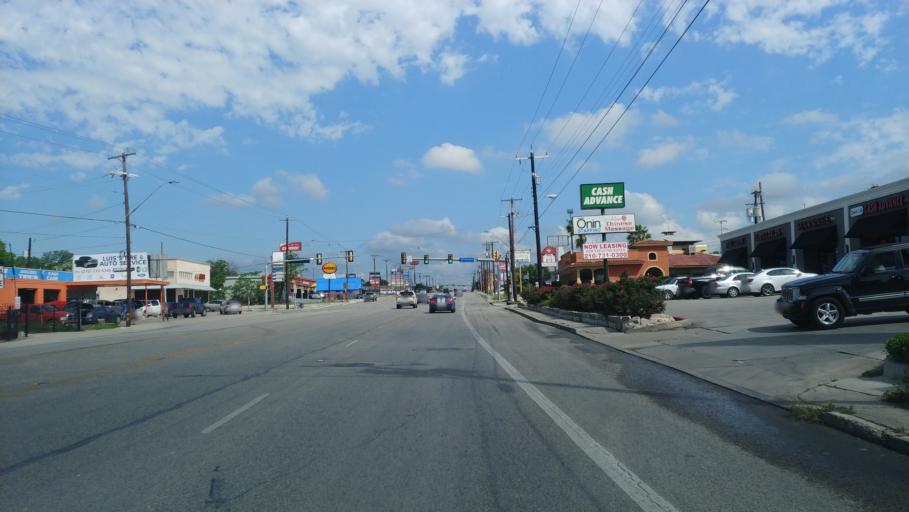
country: US
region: Texas
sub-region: Bexar County
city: Balcones Heights
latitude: 29.4808
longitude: -98.5421
